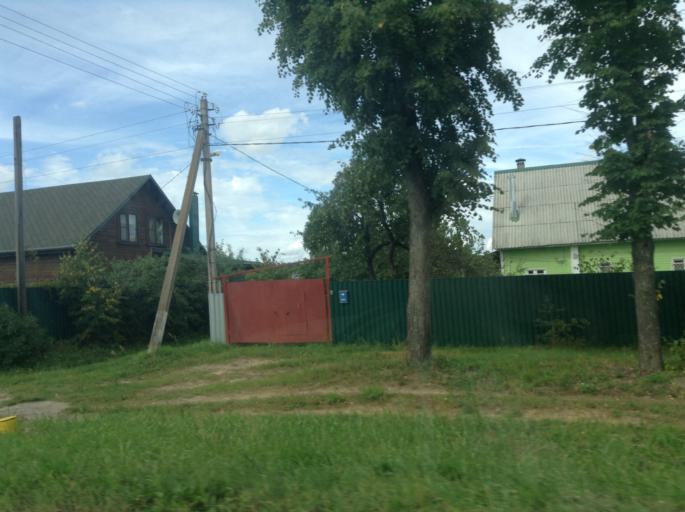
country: RU
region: Moskovskaya
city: Yegor'yevsk
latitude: 55.3529
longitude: 39.1285
